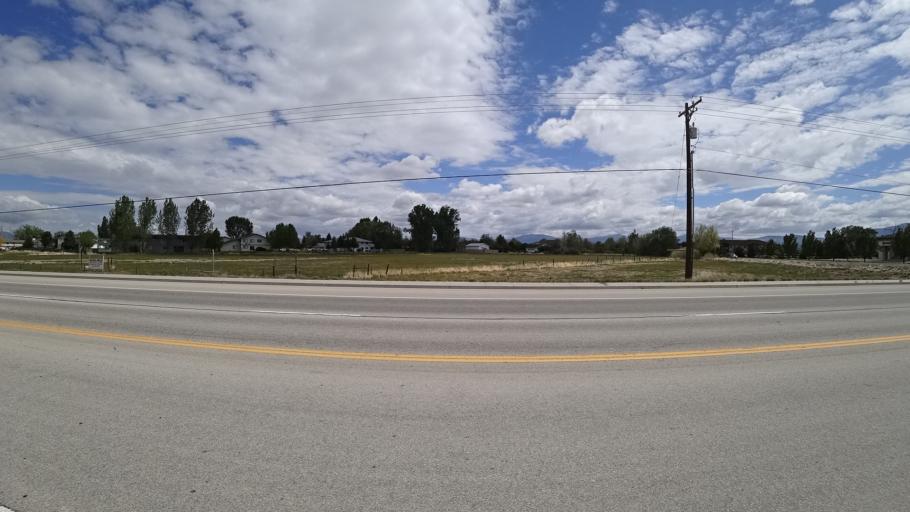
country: US
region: Nevada
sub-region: Douglas County
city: Gardnerville
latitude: 38.9332
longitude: -119.7351
